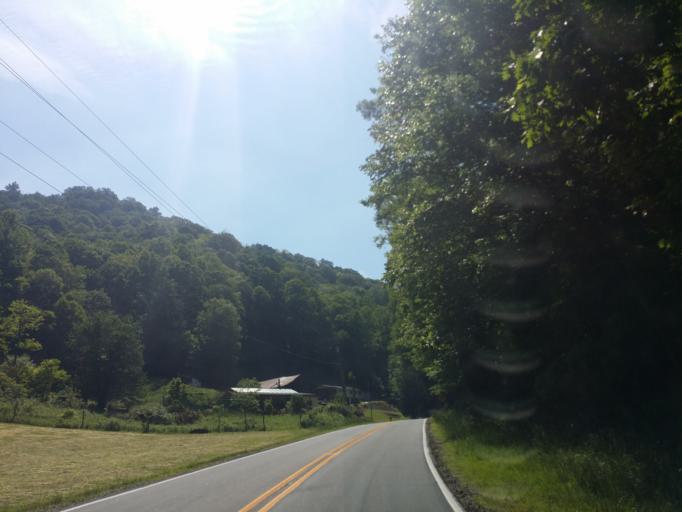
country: US
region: North Carolina
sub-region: Madison County
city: Marshall
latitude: 35.7436
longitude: -82.8446
